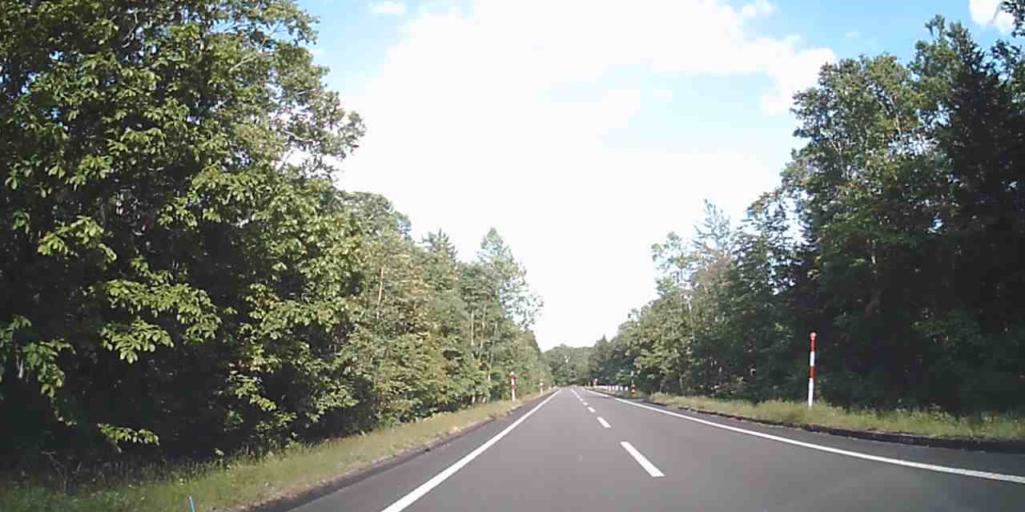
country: JP
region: Hokkaido
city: Shiraoi
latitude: 42.6814
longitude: 141.4433
